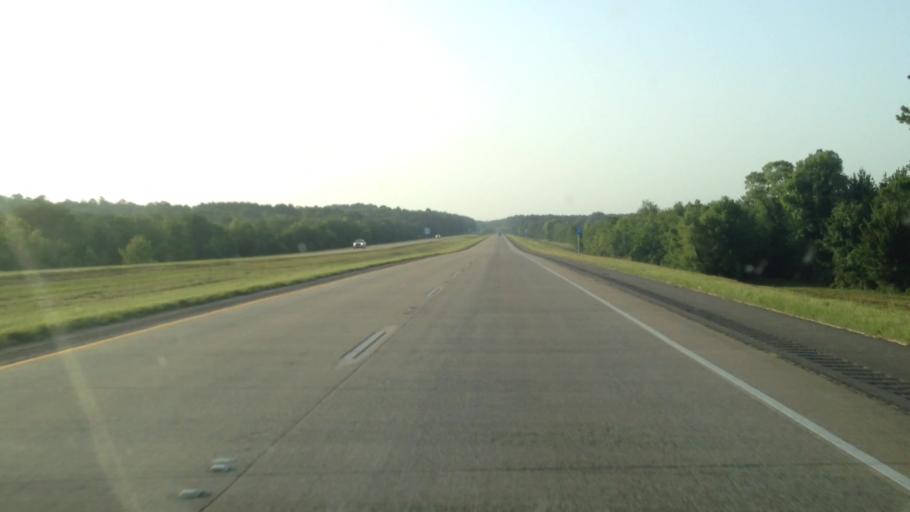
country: US
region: Louisiana
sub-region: Grant Parish
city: Colfax
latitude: 31.4887
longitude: -92.8540
